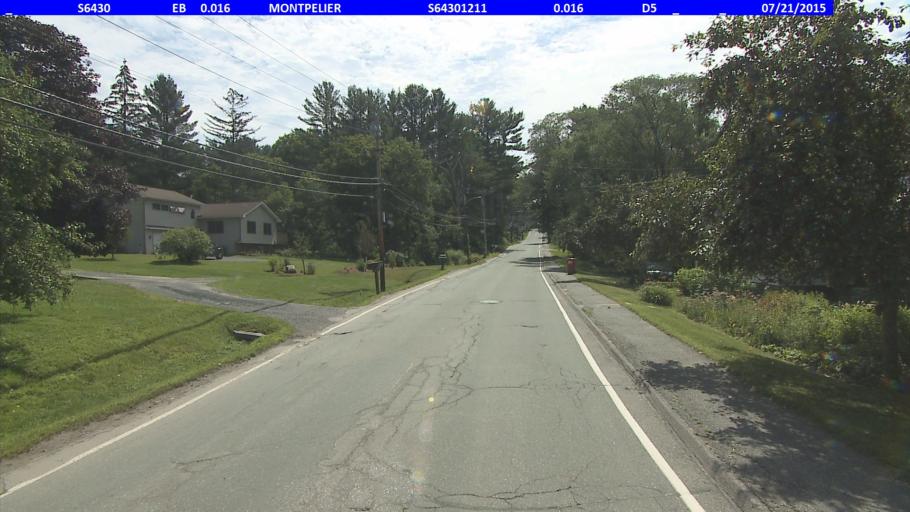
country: US
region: Vermont
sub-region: Washington County
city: Montpelier
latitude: 44.2619
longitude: -72.5580
